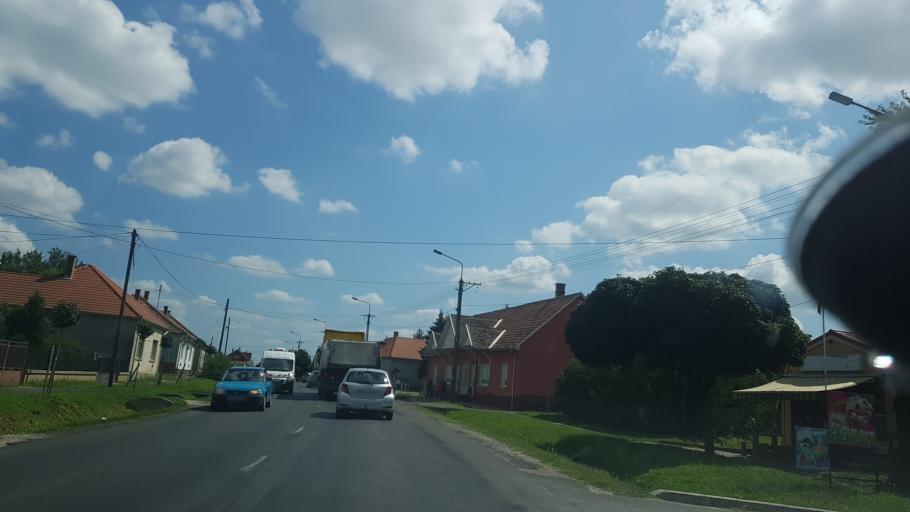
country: HU
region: Somogy
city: Kethely
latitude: 46.6413
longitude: 17.3944
